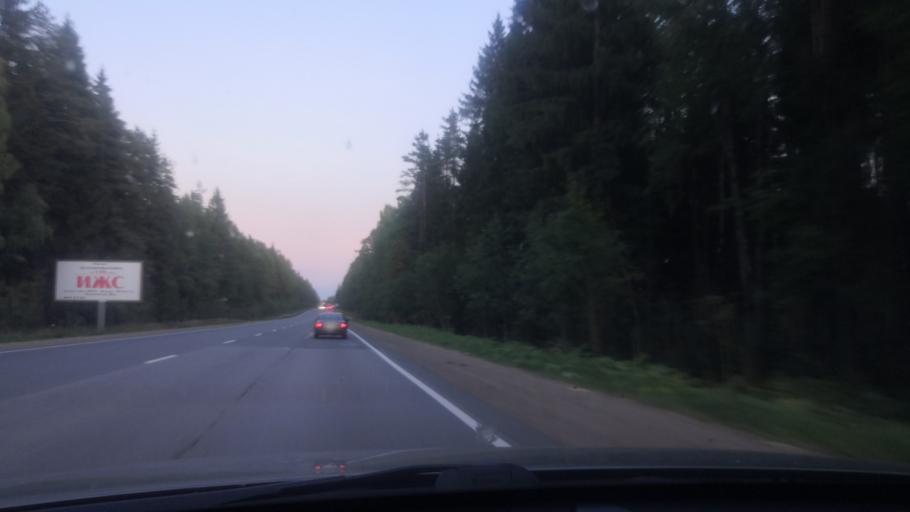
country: RU
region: St.-Petersburg
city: Pesochnyy
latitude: 60.1861
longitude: 30.1118
